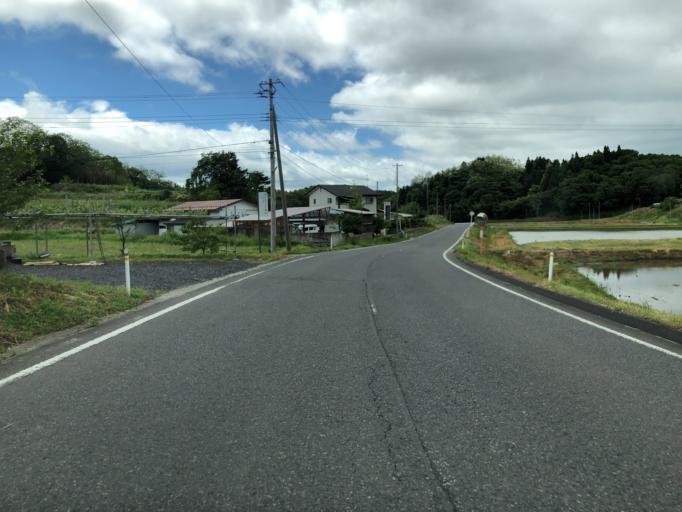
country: JP
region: Fukushima
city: Miharu
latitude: 37.4673
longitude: 140.4749
